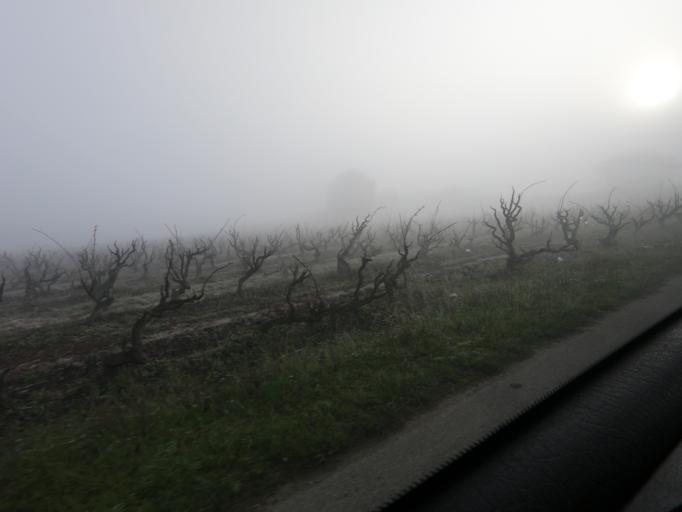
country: PT
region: Setubal
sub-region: Palmela
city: Palmela
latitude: 38.5994
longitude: -8.8458
